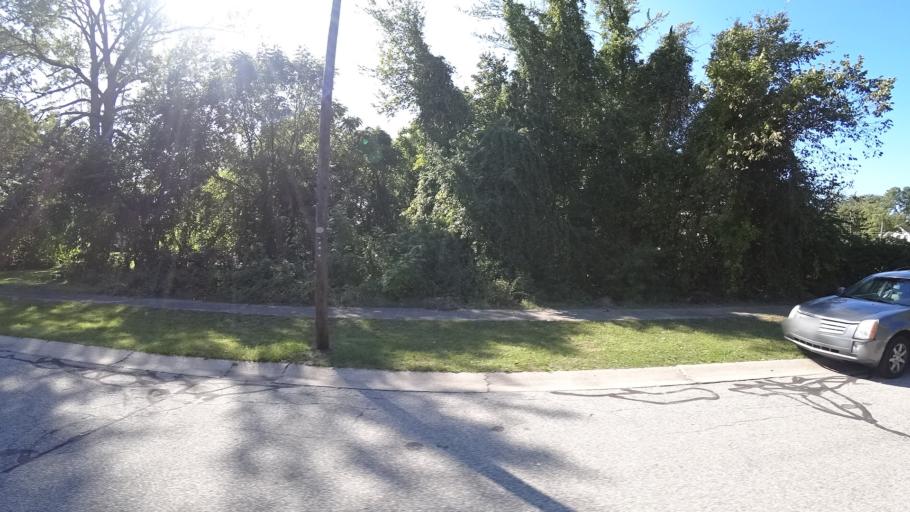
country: US
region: Indiana
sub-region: LaPorte County
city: Michigan City
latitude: 41.7103
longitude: -86.9100
